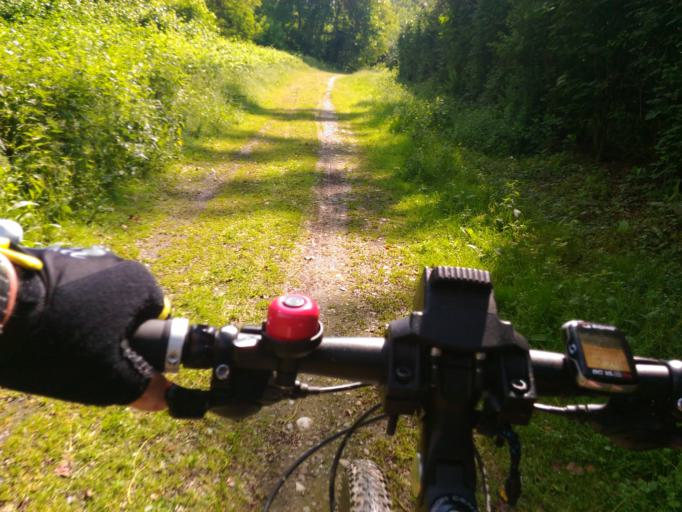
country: IT
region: Lombardy
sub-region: Provincia di Lodi
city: Massalengo-Motta Vigana
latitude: 45.2717
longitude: 9.5036
